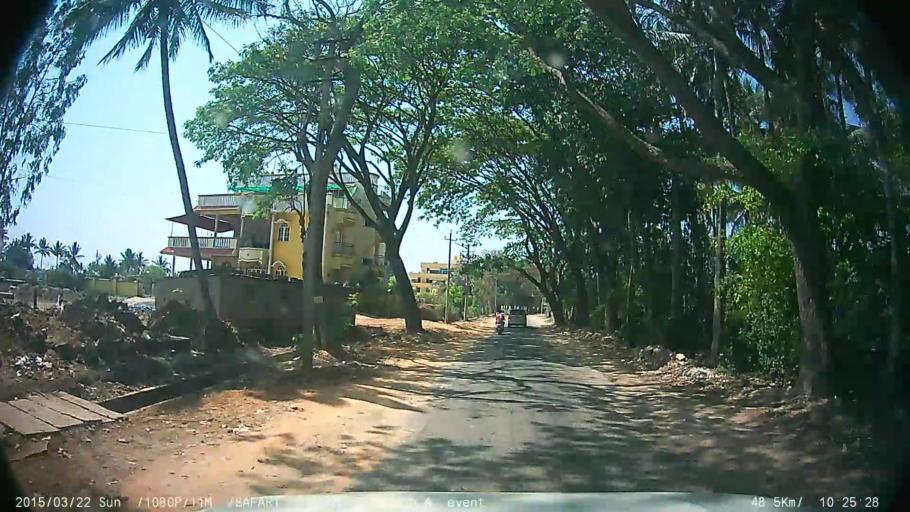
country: IN
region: Karnataka
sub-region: Bangalore Urban
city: Anekal
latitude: 12.8108
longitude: 77.5785
